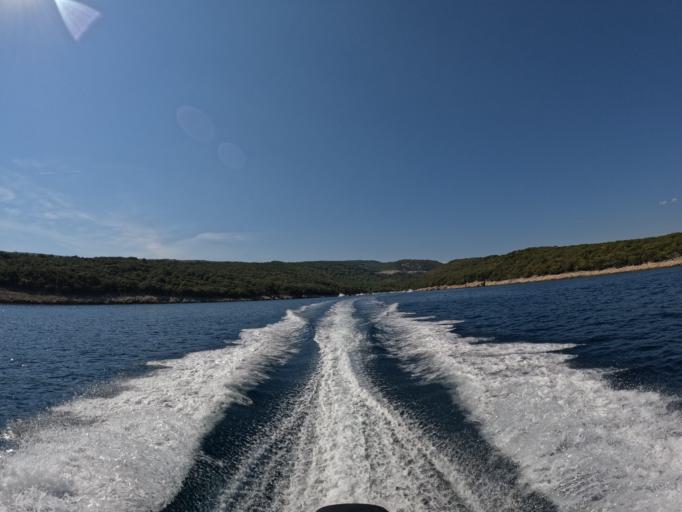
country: HR
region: Primorsko-Goranska
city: Cres
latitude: 44.9470
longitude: 14.4669
